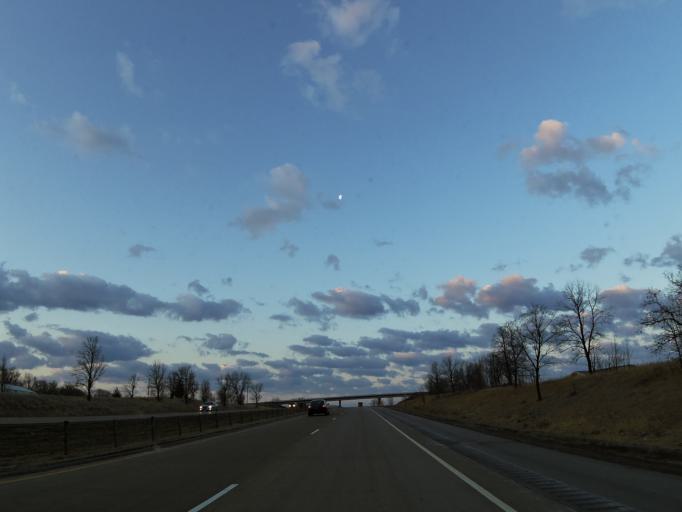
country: US
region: Minnesota
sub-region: Scott County
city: Elko New Market
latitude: 44.5068
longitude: -93.2890
